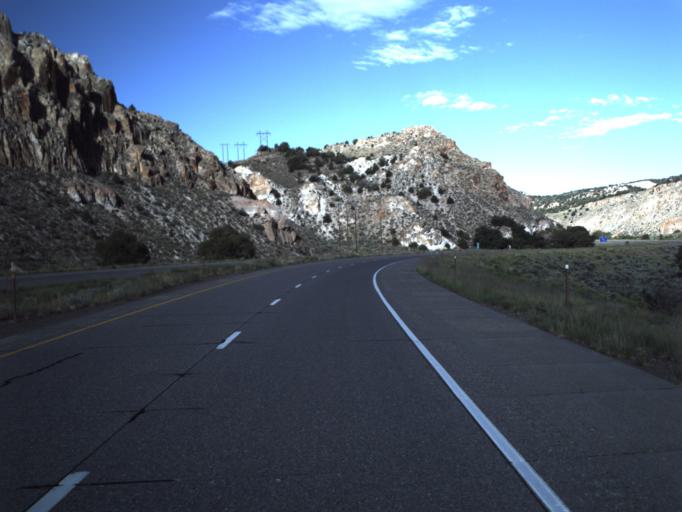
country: US
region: Utah
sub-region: Sevier County
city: Monroe
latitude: 38.5778
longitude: -112.3190
